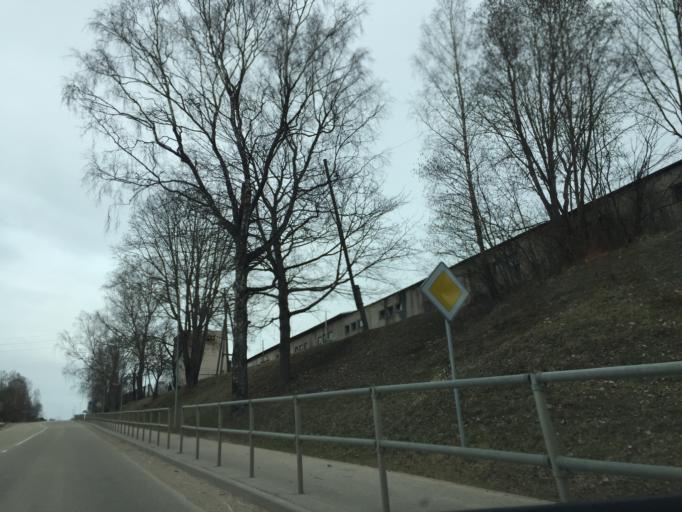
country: LV
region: Kraslavas Rajons
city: Kraslava
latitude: 55.9028
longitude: 27.1544
